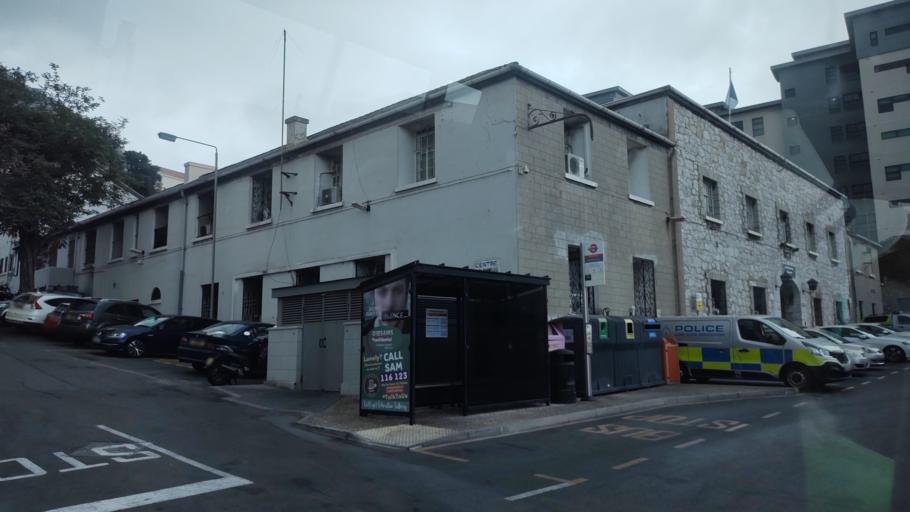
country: GI
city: Gibraltar
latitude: 36.1242
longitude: -5.3536
